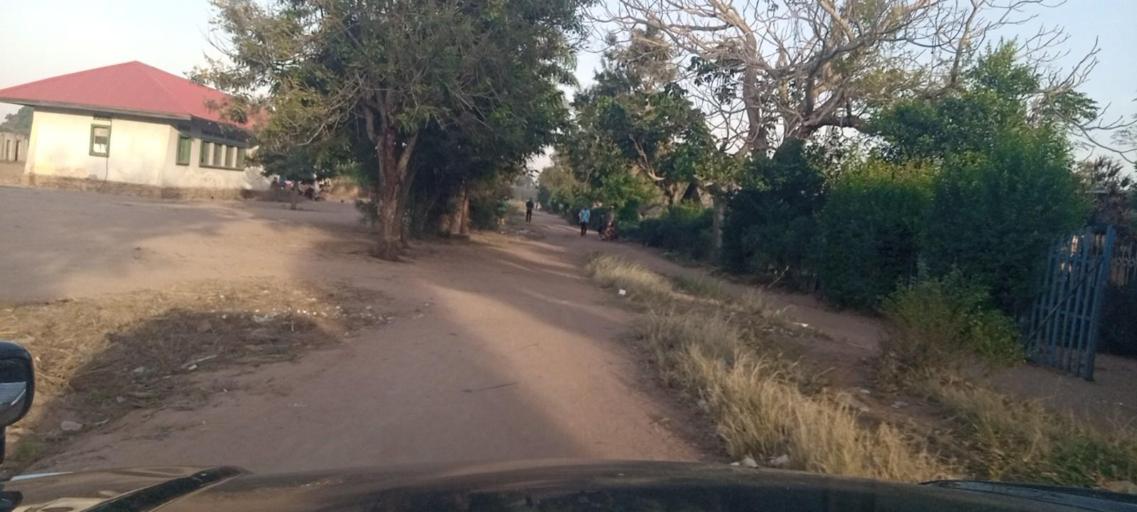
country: CD
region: Kasai-Oriental
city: Lubao
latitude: -5.3849
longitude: 25.7442
